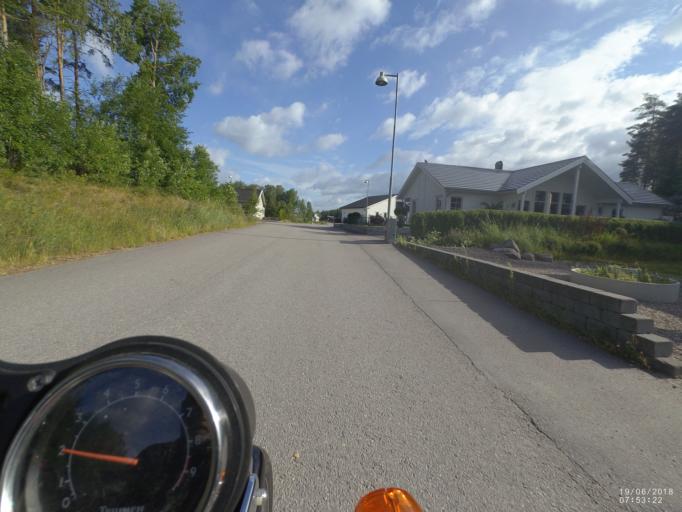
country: SE
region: Soedermanland
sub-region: Nykopings Kommun
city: Nykoping
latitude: 58.7763
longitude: 17.0081
